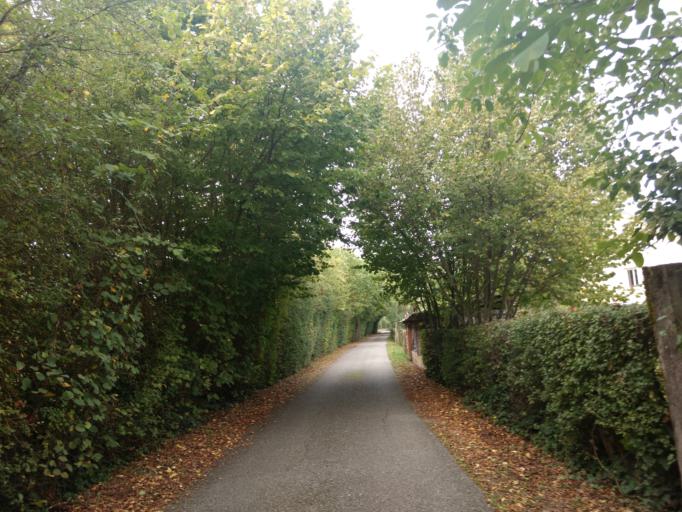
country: FR
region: Midi-Pyrenees
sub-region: Departement de l'Aveyron
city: Colombies
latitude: 44.4052
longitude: 2.2933
